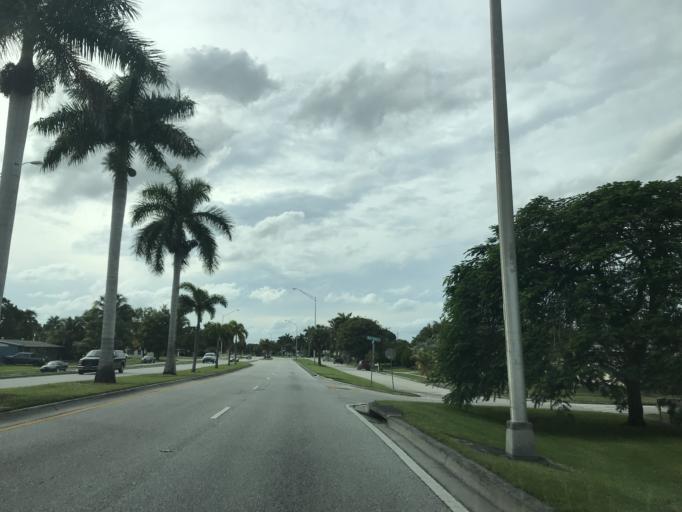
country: US
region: Florida
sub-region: Broward County
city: Margate
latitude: 26.2548
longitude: -80.2044
